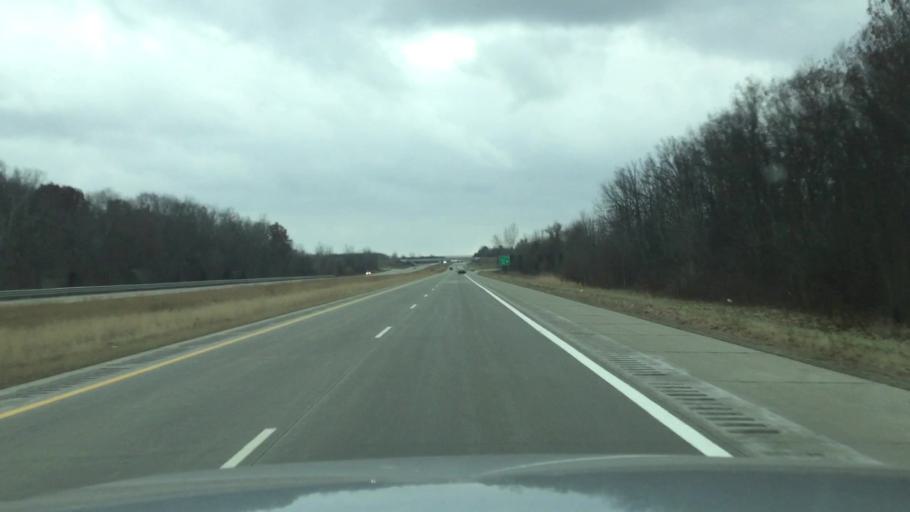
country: US
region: Michigan
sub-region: Genesee County
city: Grand Blanc
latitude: 42.9528
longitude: -83.6824
